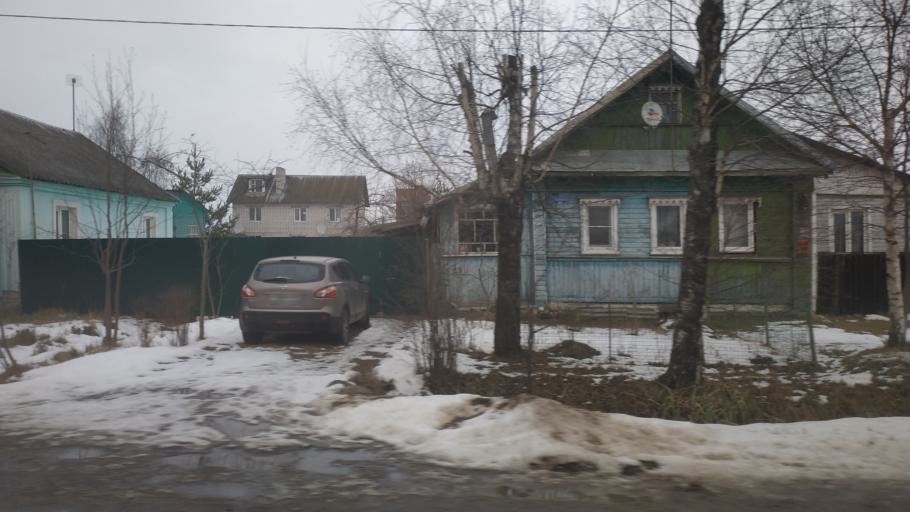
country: RU
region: Tverskaya
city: Tver
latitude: 56.8916
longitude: 35.8785
